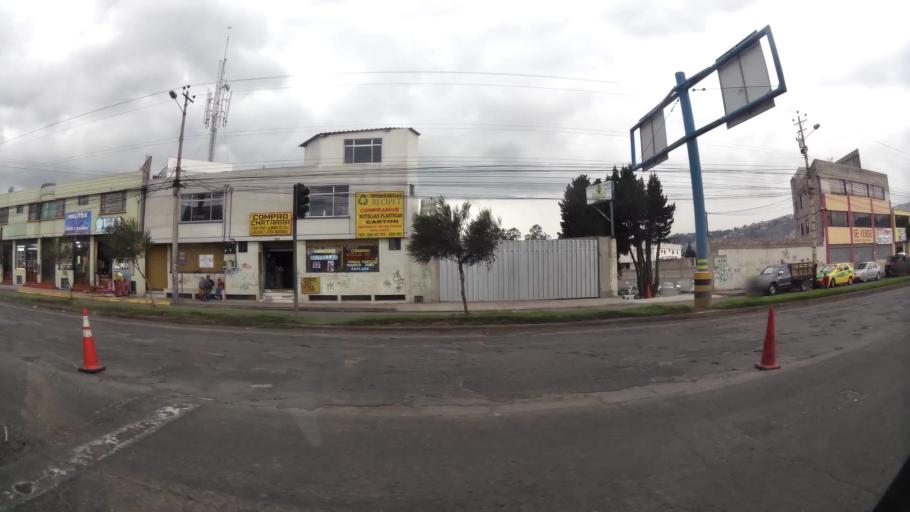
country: EC
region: Pichincha
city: Quito
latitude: -0.1071
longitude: -78.4439
